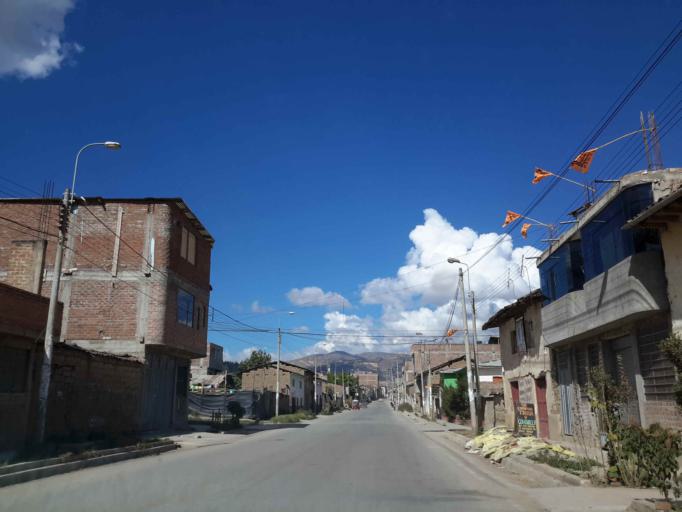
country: PE
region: Apurimac
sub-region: Provincia de Andahuaylas
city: Talavera
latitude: -13.6524
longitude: -73.4343
